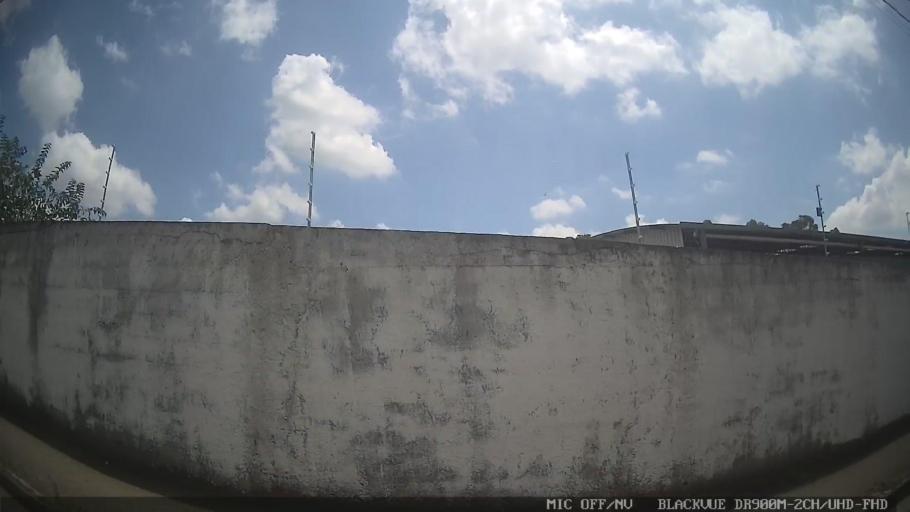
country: BR
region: Sao Paulo
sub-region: Jacarei
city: Jacarei
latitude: -23.3031
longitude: -46.0166
